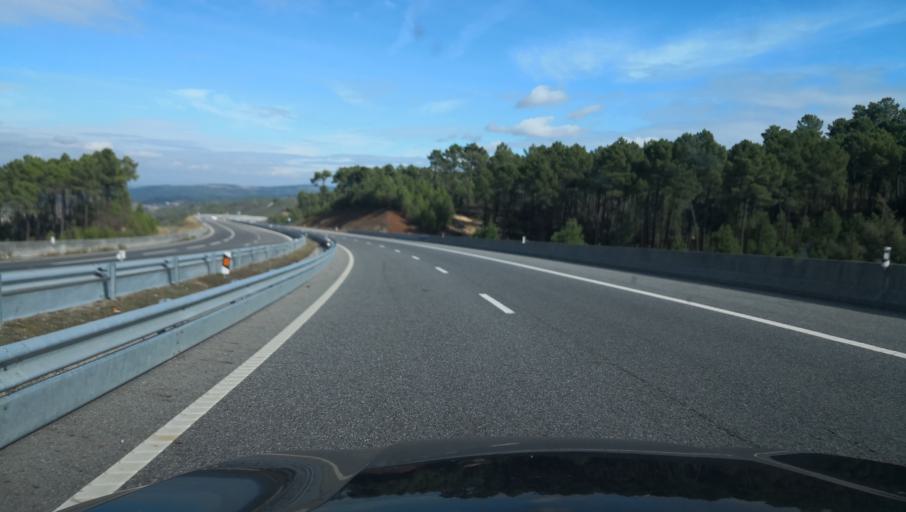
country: PT
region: Vila Real
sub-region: Boticas
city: Boticas
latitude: 41.6170
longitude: -7.6072
